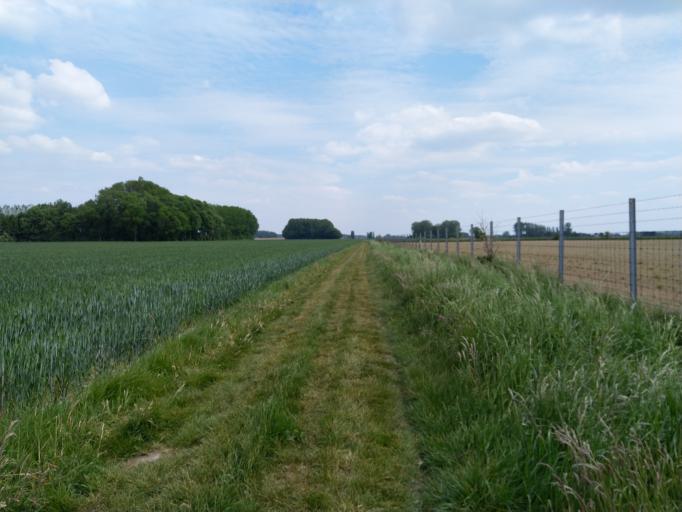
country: BE
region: Wallonia
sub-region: Province du Hainaut
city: Jurbise
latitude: 50.5464
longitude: 3.9357
